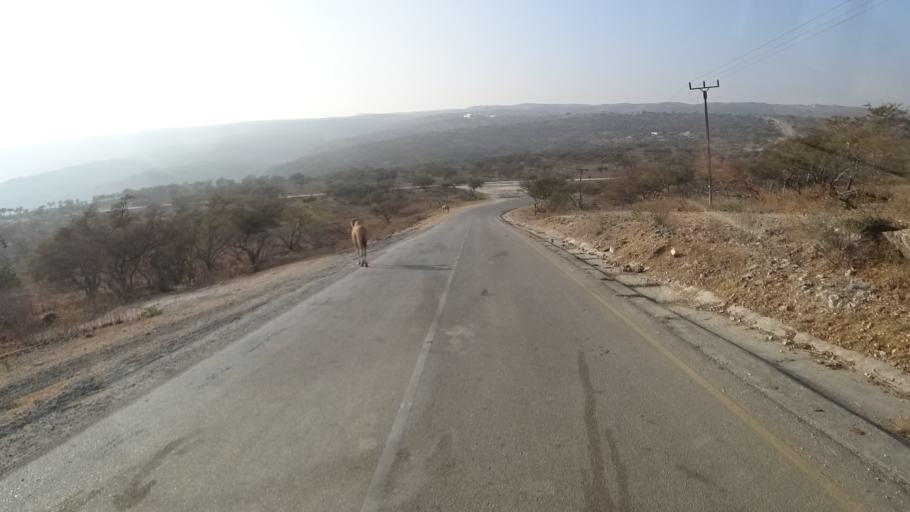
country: YE
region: Al Mahrah
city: Hawf
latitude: 16.7801
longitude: 53.3323
